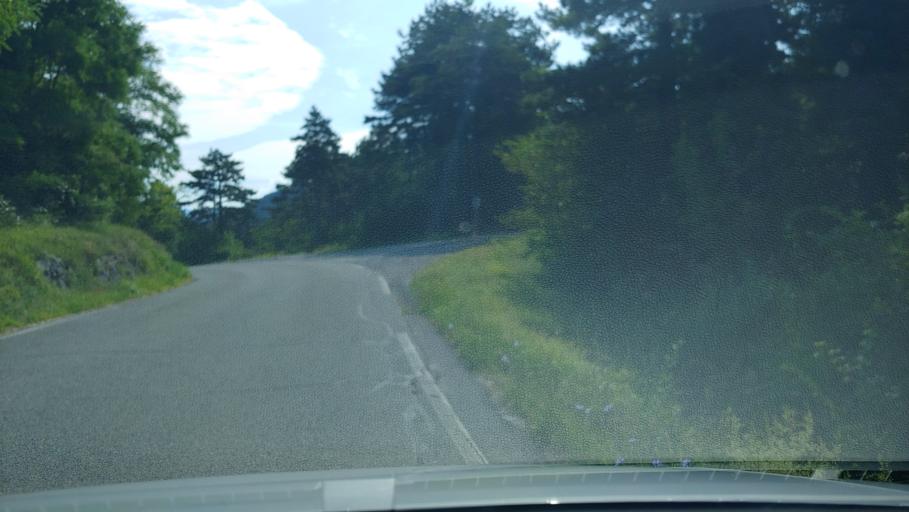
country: SI
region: Komen
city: Komen
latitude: 45.8448
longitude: 13.7801
